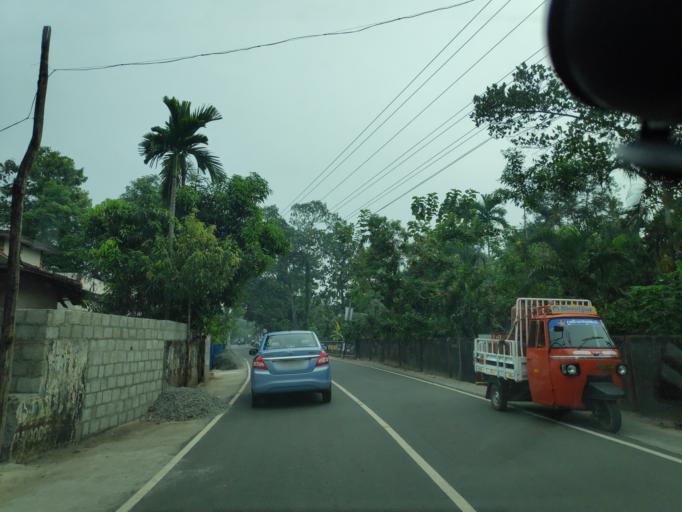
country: IN
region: Kerala
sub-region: Alappuzha
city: Shertallai
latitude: 9.6072
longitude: 76.3520
